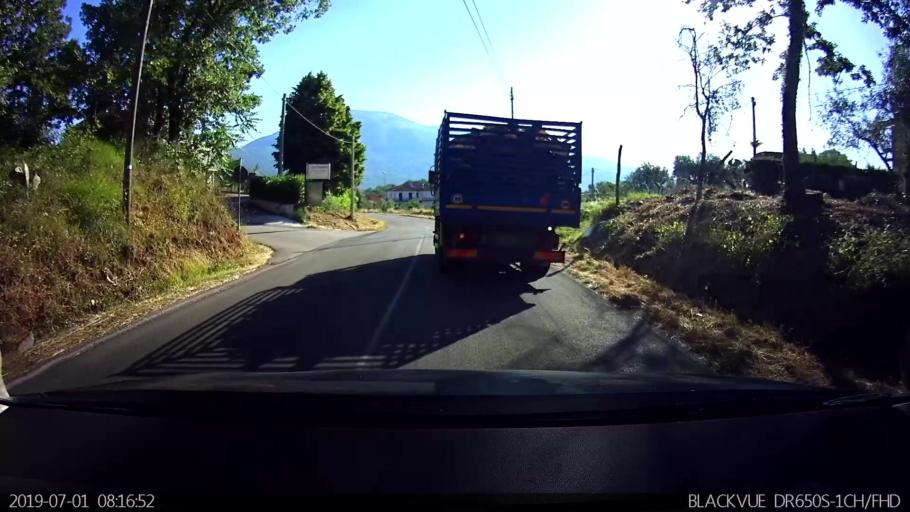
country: IT
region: Latium
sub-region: Provincia di Frosinone
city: Veroli
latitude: 41.7014
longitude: 13.4348
